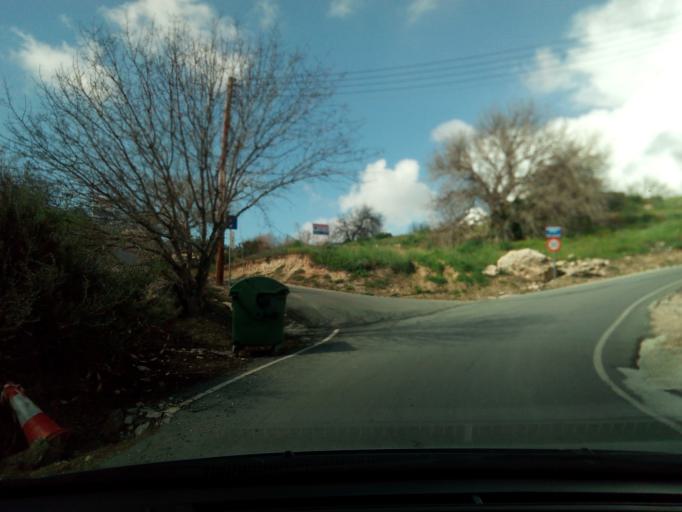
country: CY
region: Pafos
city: Mesogi
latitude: 34.8146
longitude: 32.4459
